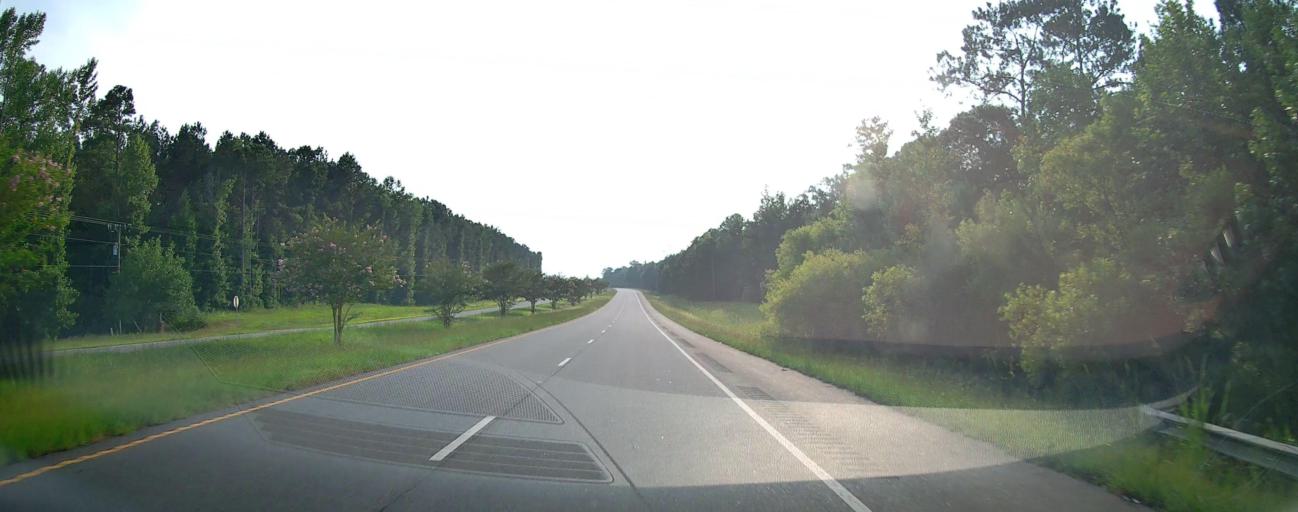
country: US
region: Georgia
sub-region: Talbot County
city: Talbotton
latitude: 32.5498
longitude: -84.6945
